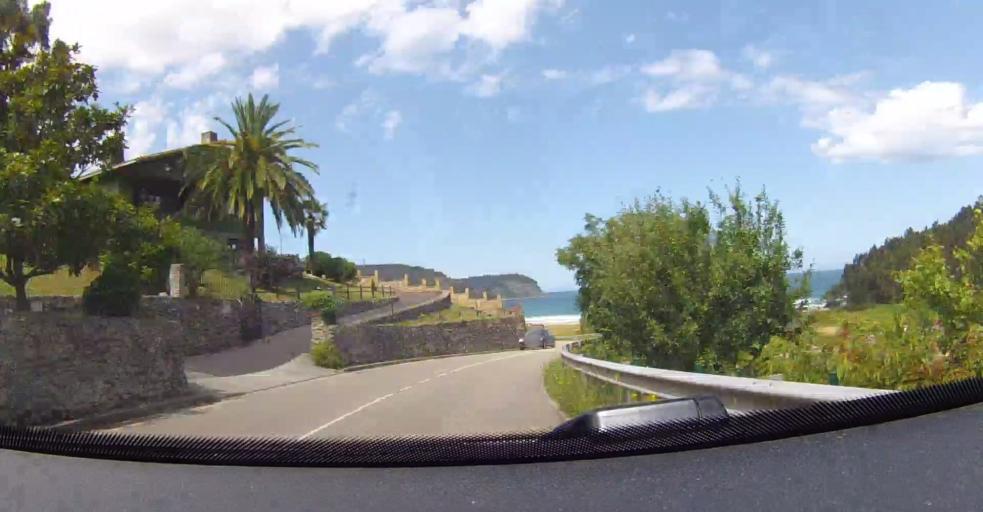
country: ES
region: Asturias
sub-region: Province of Asturias
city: Villaviciosa
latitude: 43.5307
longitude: -5.3739
